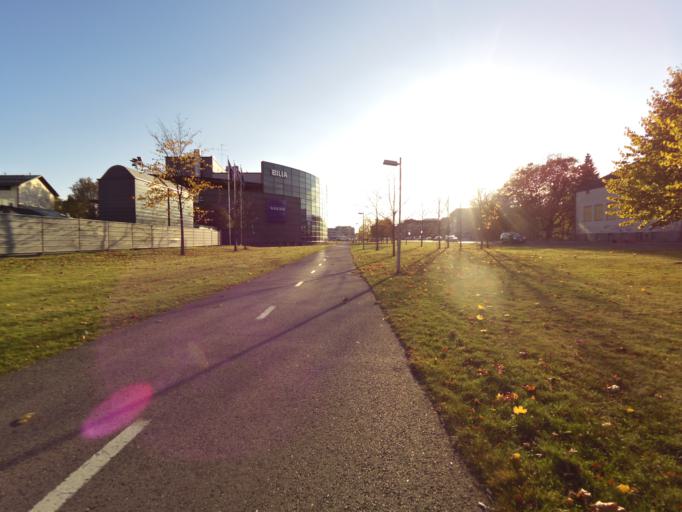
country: FI
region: Uusimaa
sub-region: Helsinki
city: Vantaa
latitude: 60.1966
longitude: 25.0398
